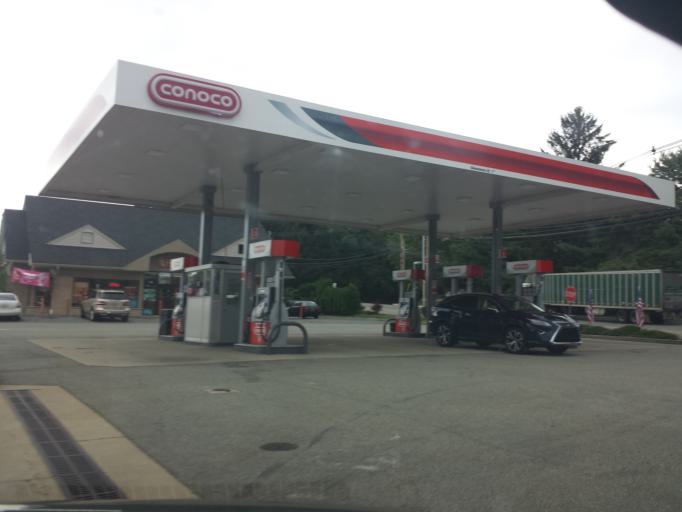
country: US
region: New Jersey
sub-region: Morris County
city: Parsippany
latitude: 40.8745
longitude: -74.4346
